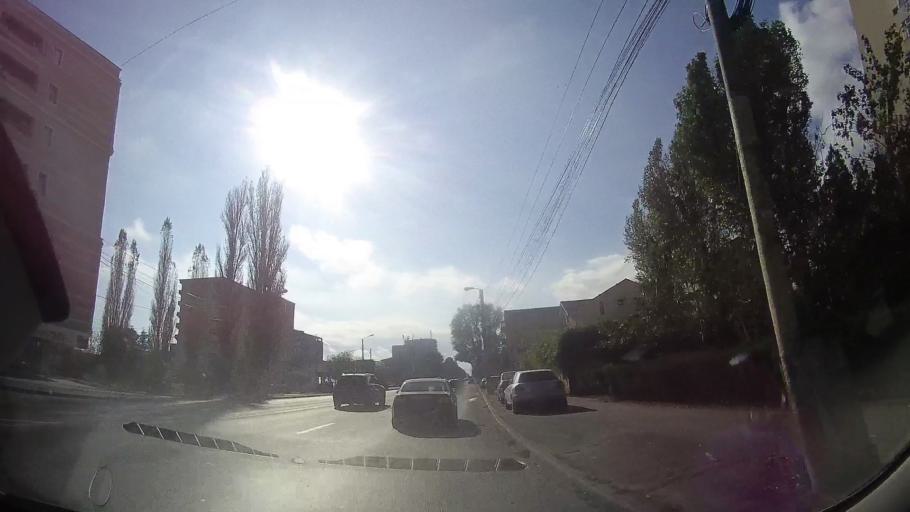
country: RO
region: Constanta
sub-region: Municipiul Constanta
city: Constanta
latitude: 44.1445
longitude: 28.6239
